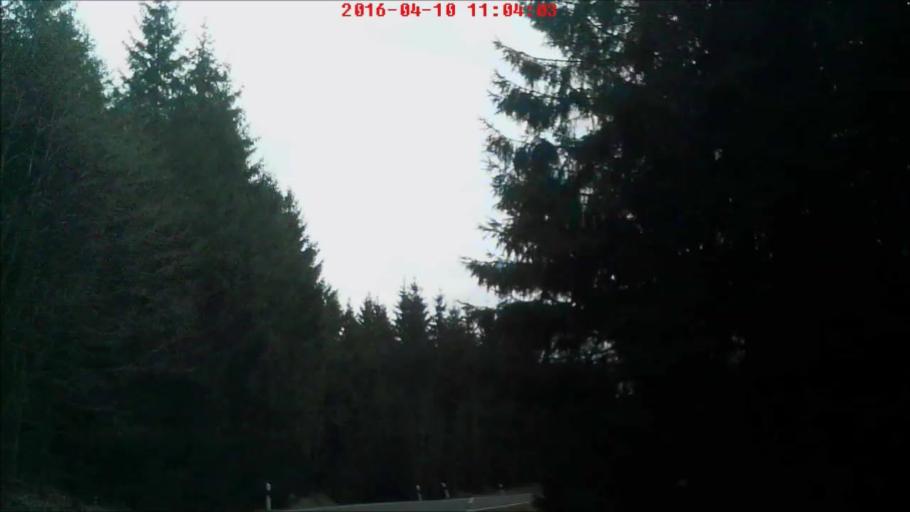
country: DE
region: Thuringia
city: Schmiedefeld am Rennsteig
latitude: 50.6029
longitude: 10.8433
